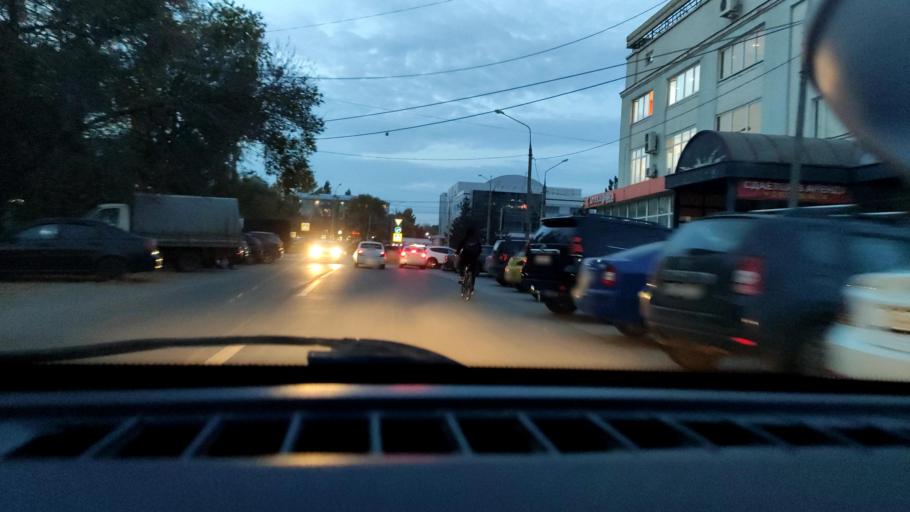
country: RU
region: Samara
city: Samara
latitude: 53.1998
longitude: 50.1985
